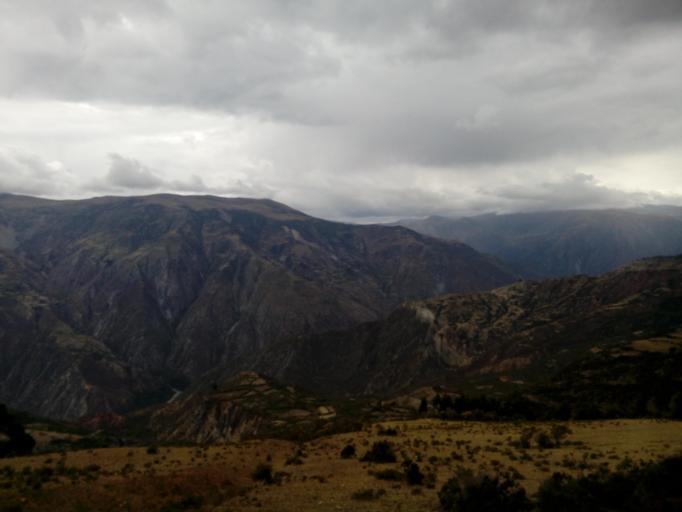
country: PE
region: Ayacucho
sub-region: Provincia de Victor Fajardo
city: Canaria
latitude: -13.8857
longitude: -73.9365
